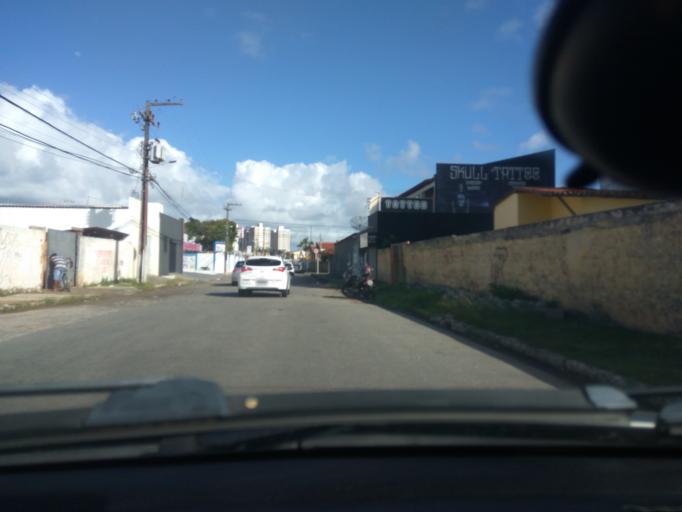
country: BR
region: Sergipe
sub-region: Aracaju
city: Aracaju
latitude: -10.9454
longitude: -37.0627
